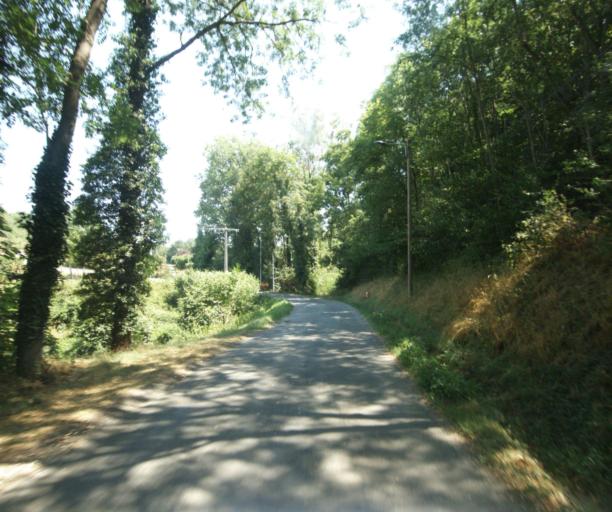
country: FR
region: Rhone-Alpes
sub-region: Departement du Rhone
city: Sourcieux-les-Mines
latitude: 45.7994
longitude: 4.6349
